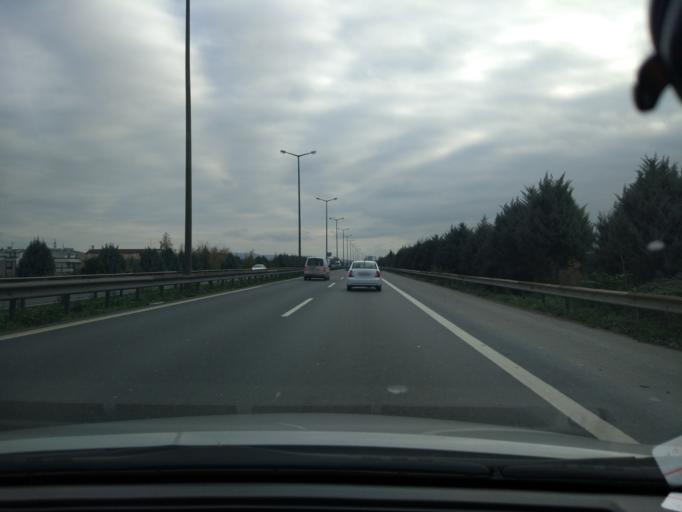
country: TR
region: Kocaeli
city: Kosekoy
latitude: 40.7700
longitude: 30.0055
